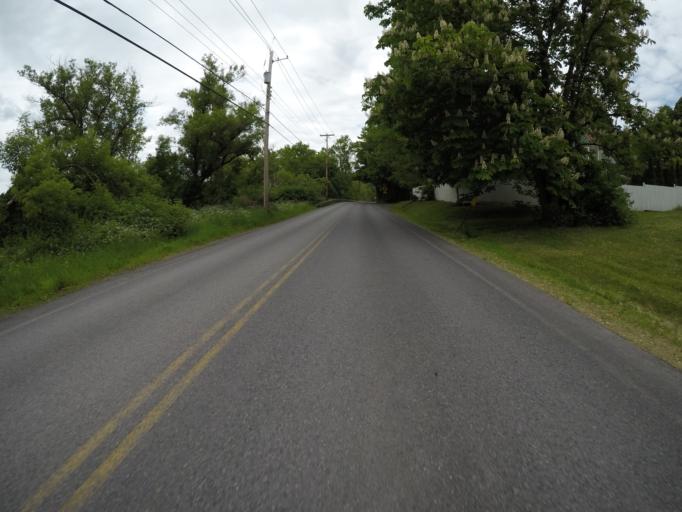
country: US
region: New York
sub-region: Delaware County
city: Stamford
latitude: 42.1499
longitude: -74.6197
